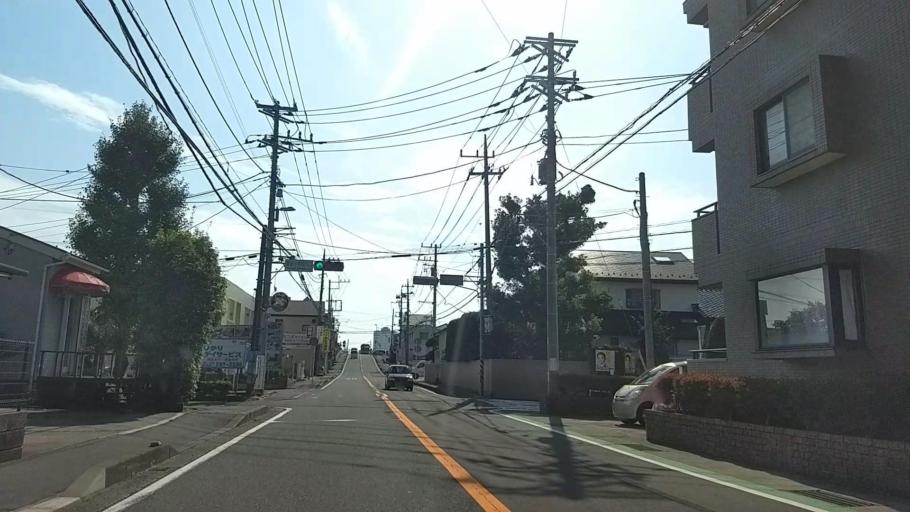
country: JP
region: Kanagawa
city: Atsugi
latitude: 35.4529
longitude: 139.3598
